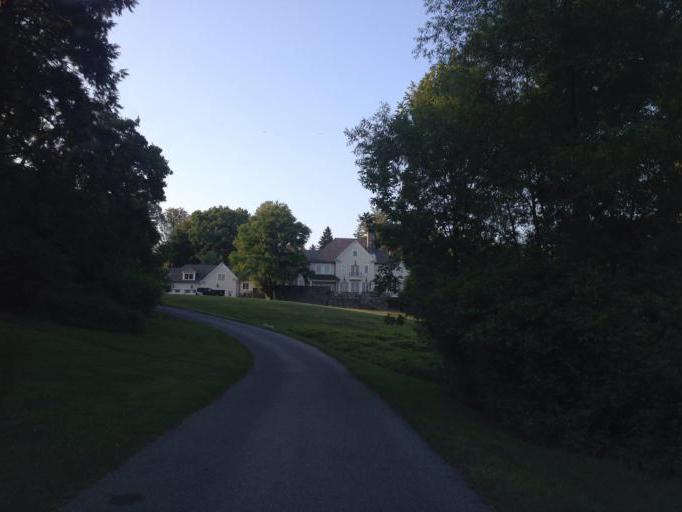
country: US
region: Maryland
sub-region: Baltimore County
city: Towson
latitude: 39.3832
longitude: -76.6354
